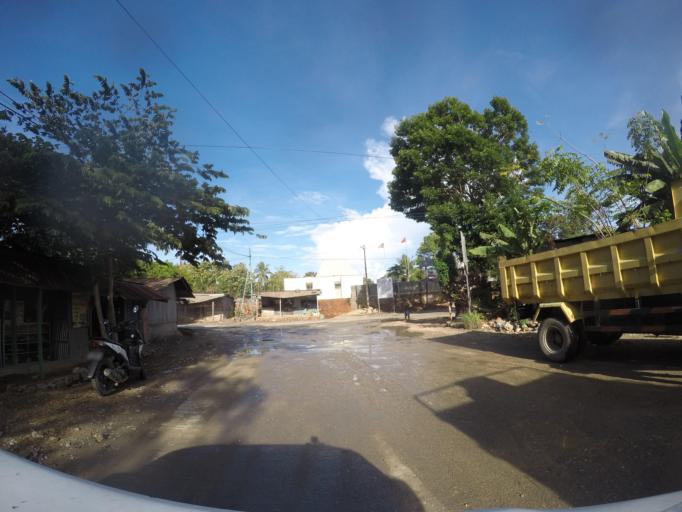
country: TL
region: Baucau
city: Baucau
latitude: -8.4838
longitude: 126.4569
